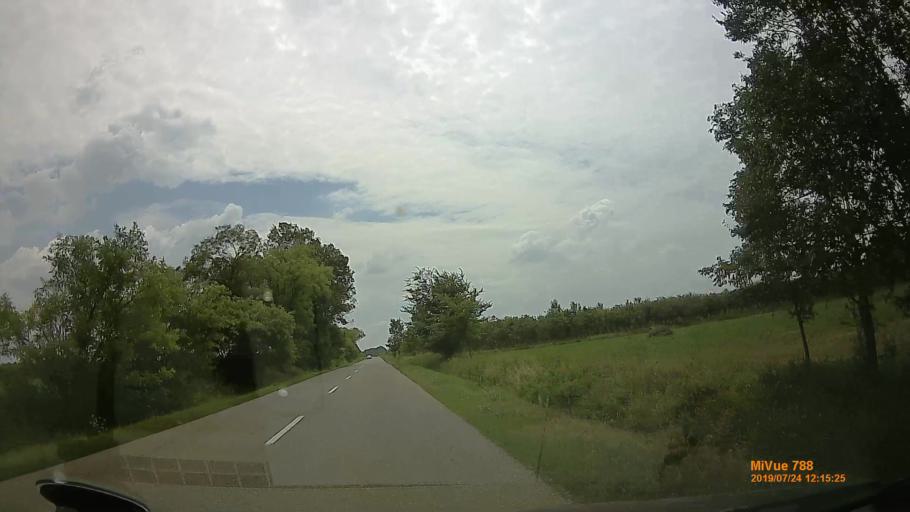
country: HU
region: Szabolcs-Szatmar-Bereg
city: Vasarosnameny
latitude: 48.1846
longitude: 22.3449
